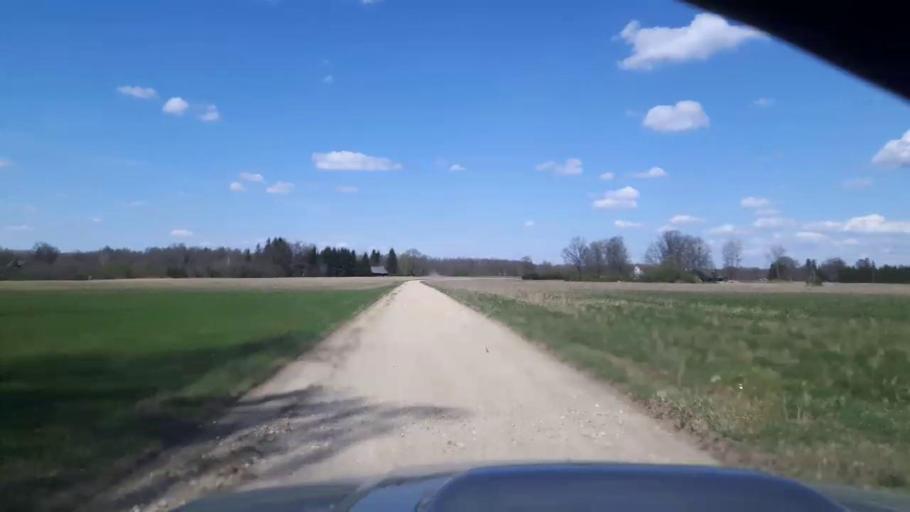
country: EE
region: Paernumaa
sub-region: Tootsi vald
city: Tootsi
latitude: 58.5004
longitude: 24.8433
